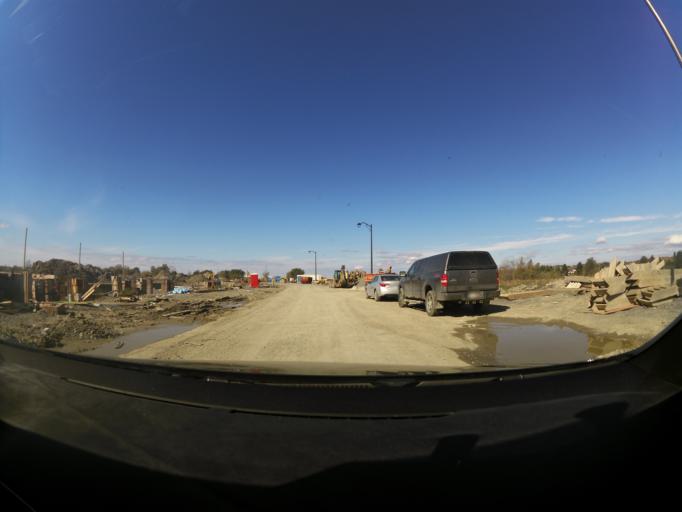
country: CA
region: Ontario
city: Bells Corners
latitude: 45.2852
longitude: -75.8919
